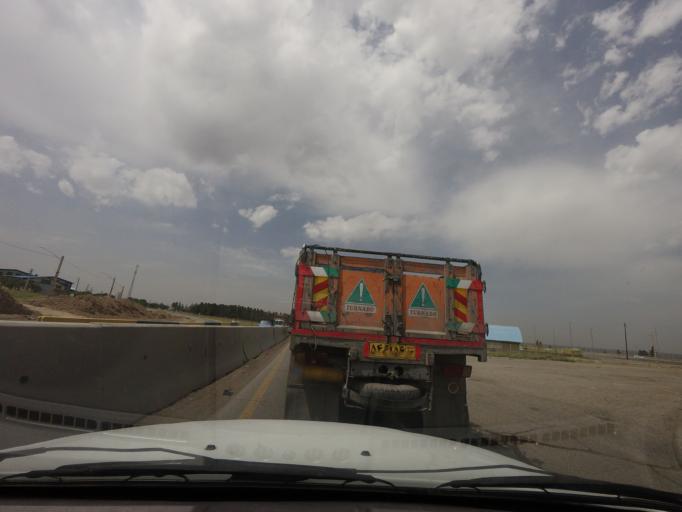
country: IR
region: Tehran
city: Shahrak-e Emam Hasan-e Mojtaba
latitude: 35.5085
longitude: 51.2968
